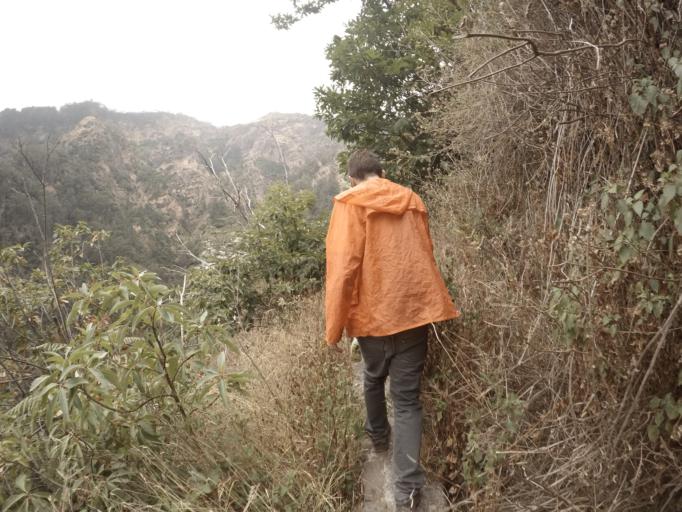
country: PT
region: Madeira
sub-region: Camara de Lobos
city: Curral das Freiras
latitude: 32.7060
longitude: -16.9688
